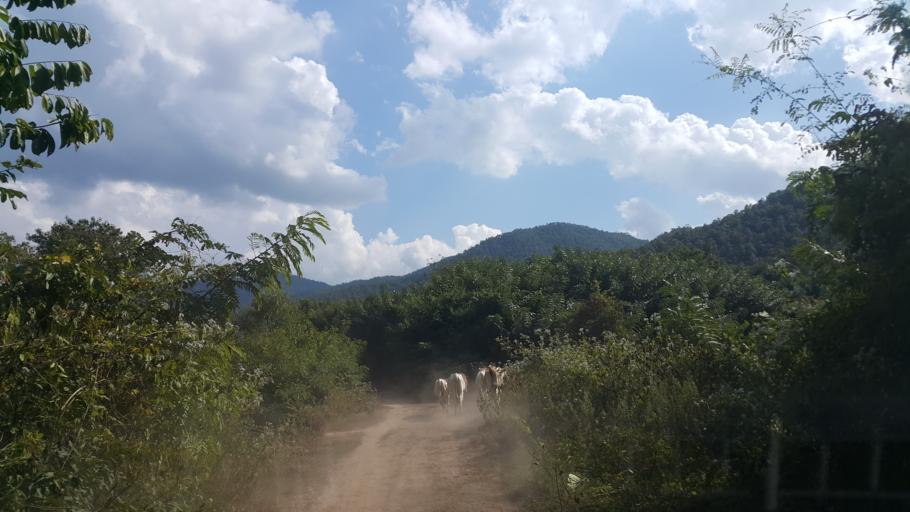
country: TH
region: Lamphun
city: Ban Thi
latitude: 18.5747
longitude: 99.1710
